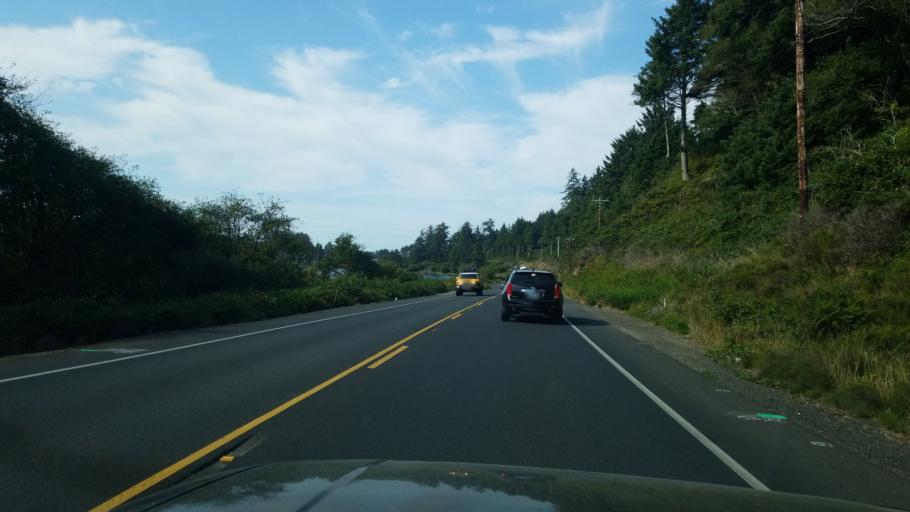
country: US
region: Oregon
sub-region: Tillamook County
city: Rockaway Beach
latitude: 45.5780
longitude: -123.9453
